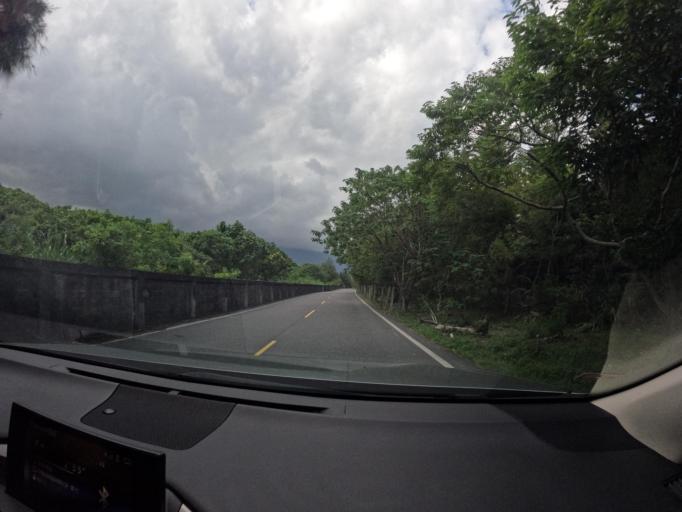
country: TW
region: Taiwan
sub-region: Hualien
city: Hualian
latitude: 24.0432
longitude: 121.6194
